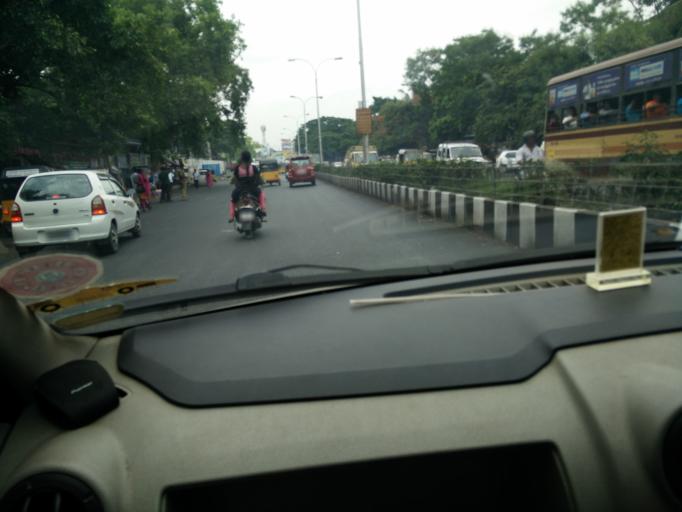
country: IN
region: Tamil Nadu
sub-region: Chennai
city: Chennai
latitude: 13.0752
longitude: 80.2763
